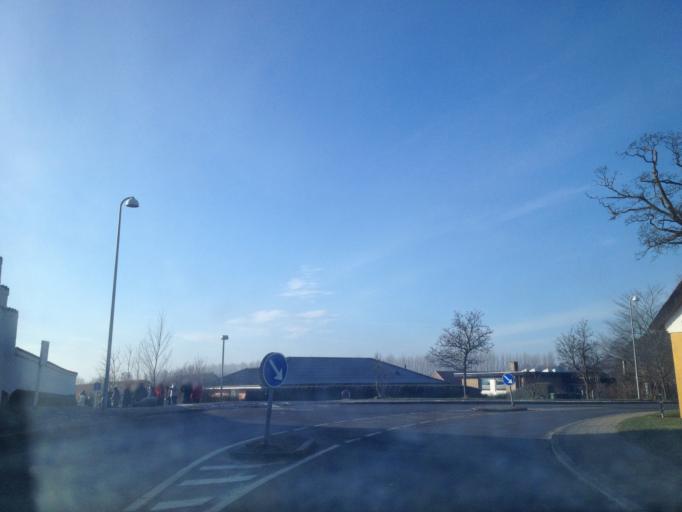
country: DK
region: Zealand
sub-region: Greve Kommune
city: Greve
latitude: 55.6078
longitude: 12.2756
